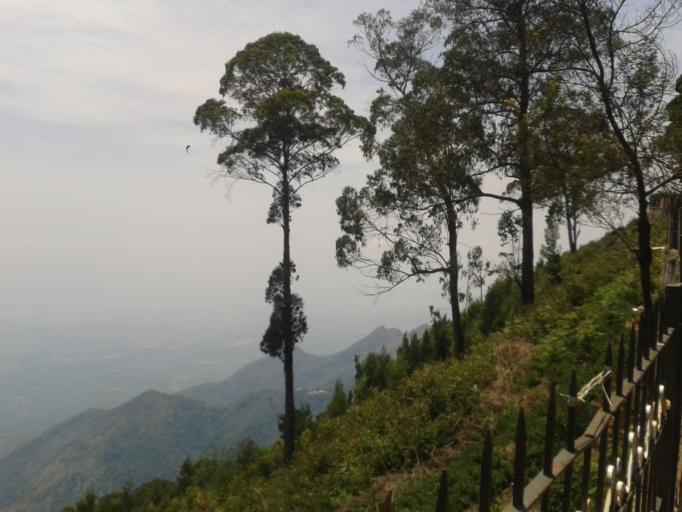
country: IN
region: Tamil Nadu
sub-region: Dindigul
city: Kodaikanal
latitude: 10.2299
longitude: 77.4936
